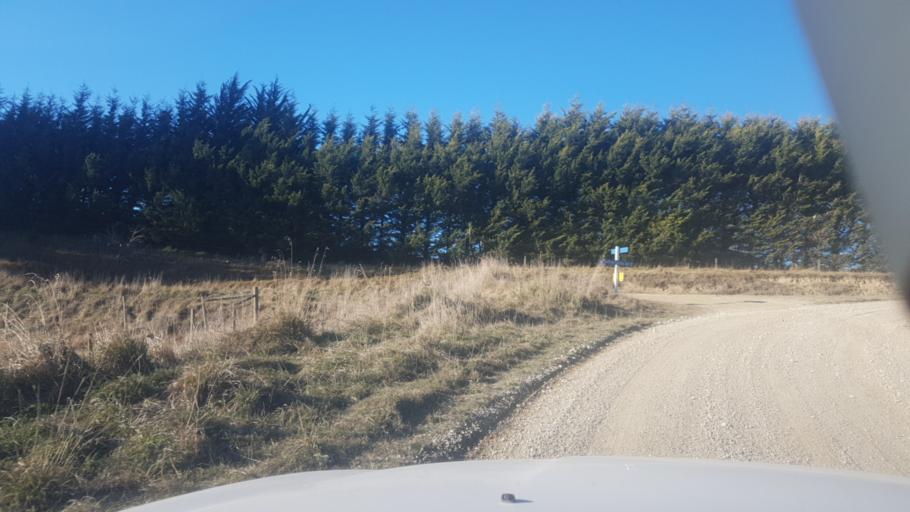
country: NZ
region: Canterbury
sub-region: Timaru District
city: Pleasant Point
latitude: -44.3426
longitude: 171.0711
